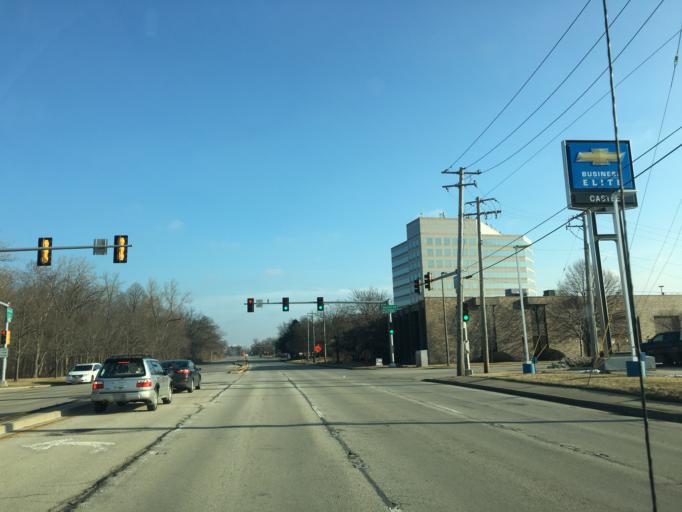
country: US
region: Illinois
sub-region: Cook County
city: Elk Grove Village
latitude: 42.0307
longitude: -87.9861
